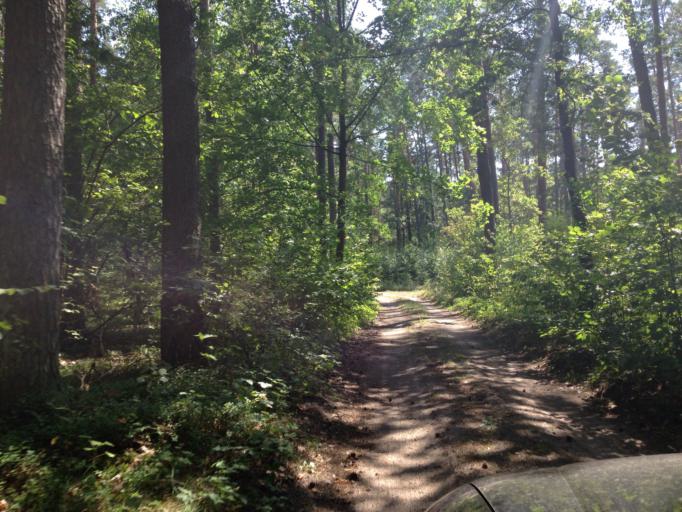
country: PL
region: Kujawsko-Pomorskie
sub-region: Powiat brodnicki
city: Bartniczka
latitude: 53.2706
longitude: 19.5708
